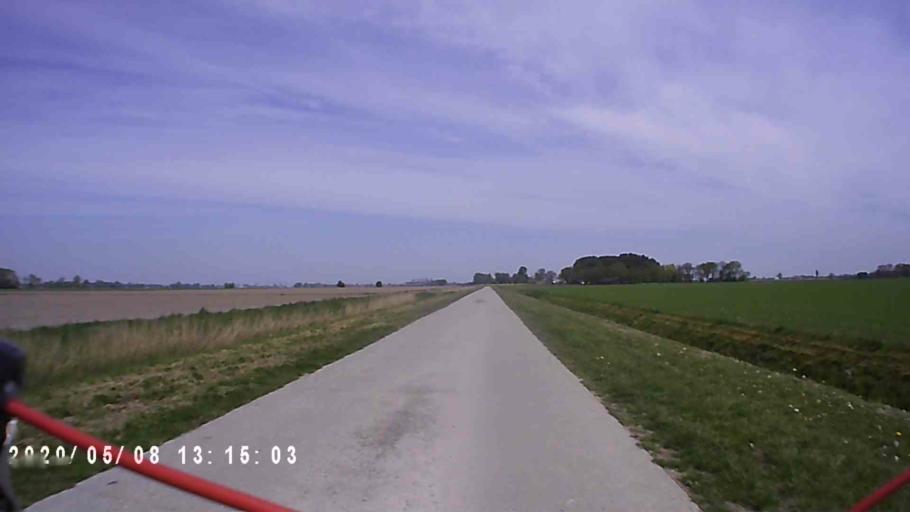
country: NL
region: Groningen
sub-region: Gemeente Bedum
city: Bedum
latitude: 53.3037
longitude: 6.6996
